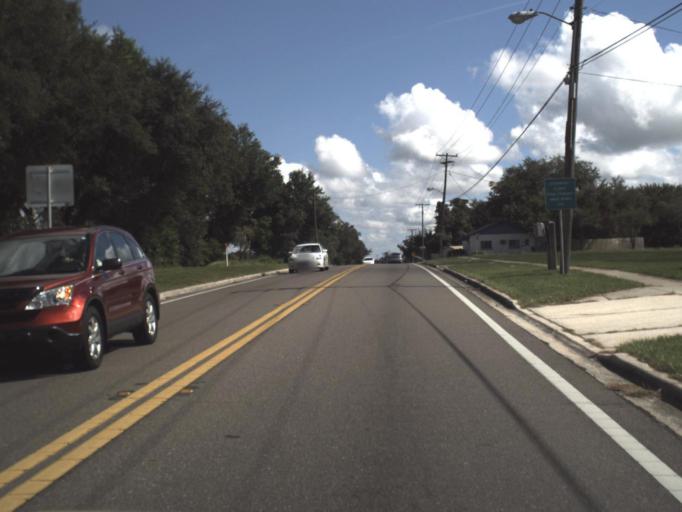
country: US
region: Florida
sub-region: Polk County
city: Davenport
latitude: 28.1545
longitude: -81.6068
